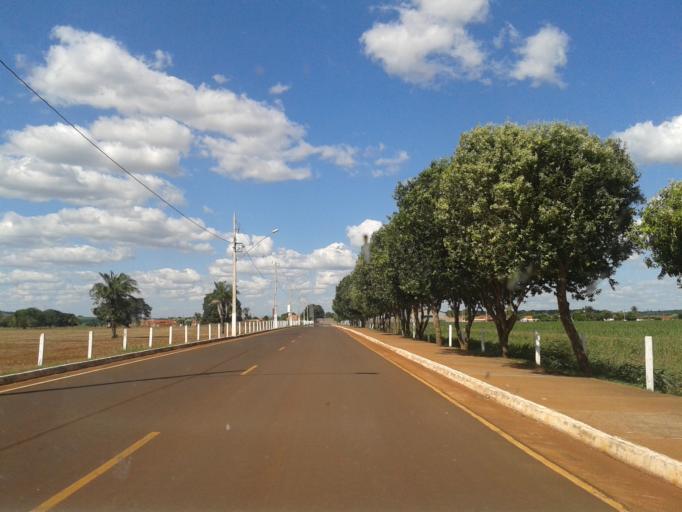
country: BR
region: Minas Gerais
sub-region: Santa Vitoria
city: Santa Vitoria
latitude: -18.6921
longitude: -49.9539
